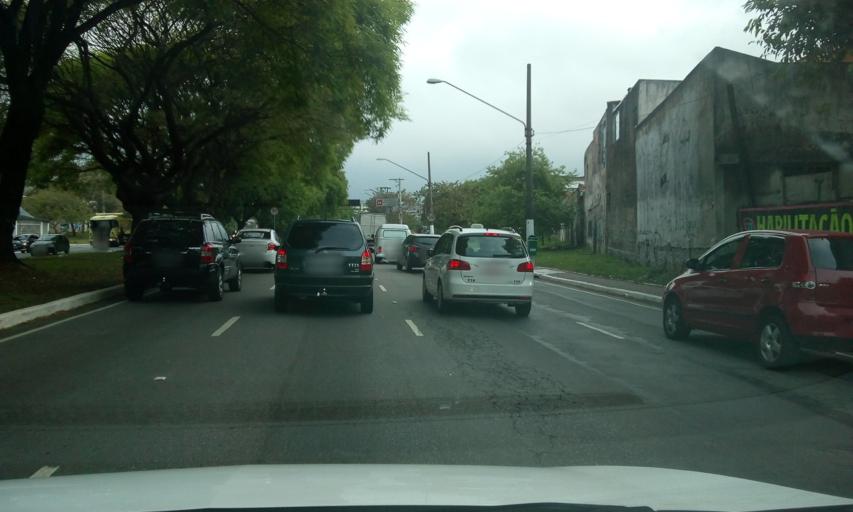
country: BR
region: Sao Paulo
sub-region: Sao Caetano Do Sul
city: Sao Caetano do Sul
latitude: -23.6196
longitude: -46.6110
